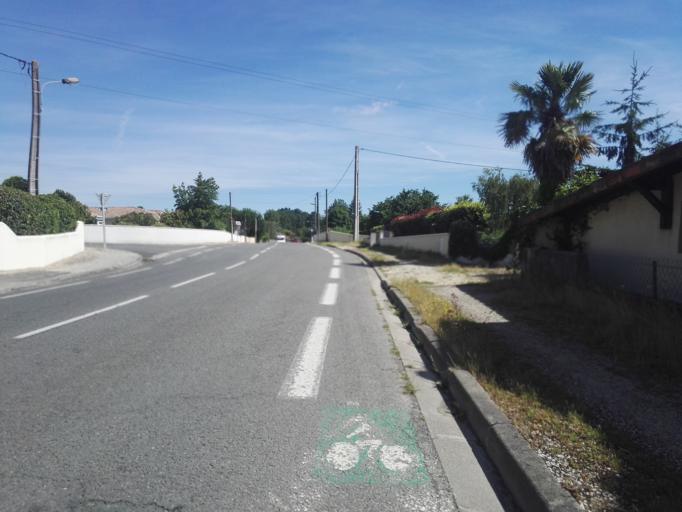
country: FR
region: Aquitaine
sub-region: Departement de la Gironde
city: Leognan
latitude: 44.7424
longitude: -0.5882
